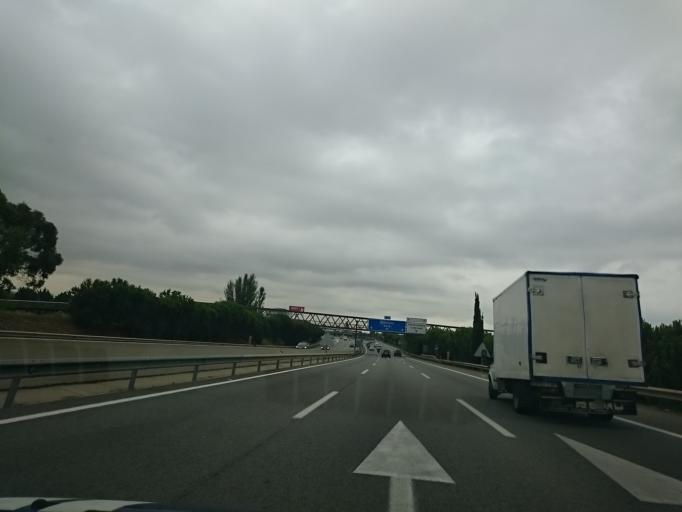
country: ES
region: Catalonia
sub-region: Provincia de Barcelona
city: Castelldefels
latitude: 41.2758
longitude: 1.9813
